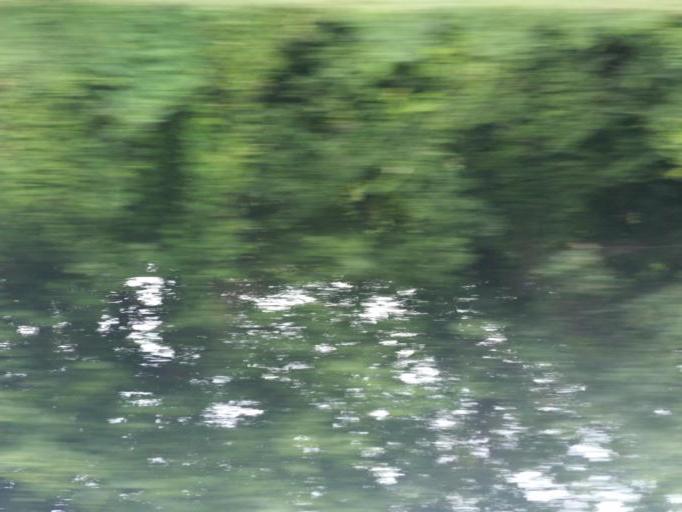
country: US
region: Kentucky
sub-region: Ballard County
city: Wickliffe
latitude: 36.9858
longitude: -89.1081
